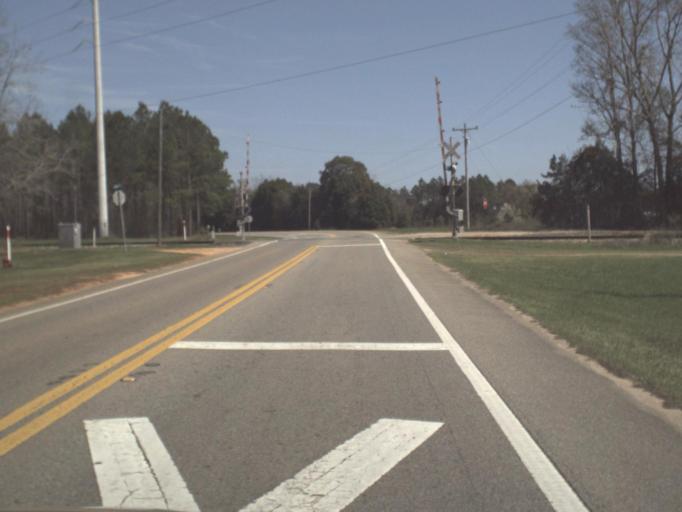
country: US
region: Florida
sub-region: Gadsden County
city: Gretna
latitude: 30.5636
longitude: -84.7466
